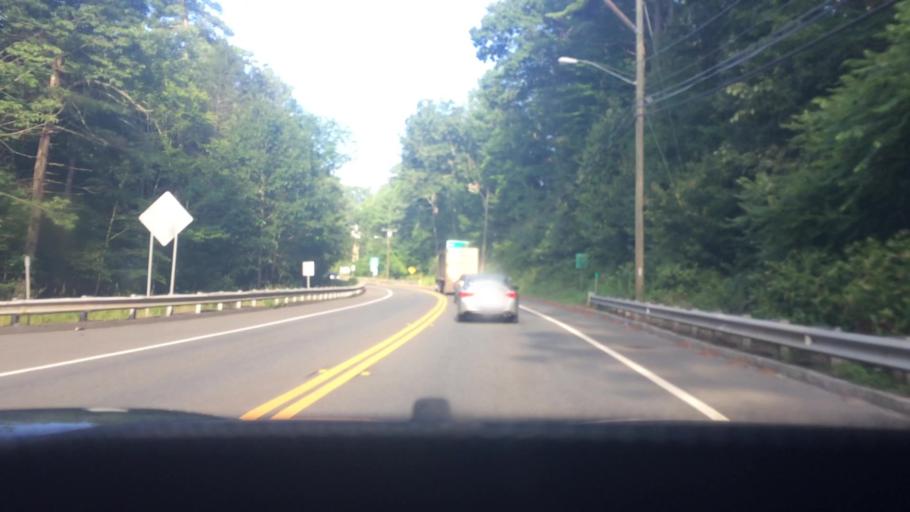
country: US
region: Massachusetts
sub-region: Franklin County
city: Turners Falls
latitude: 42.6168
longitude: -72.5563
